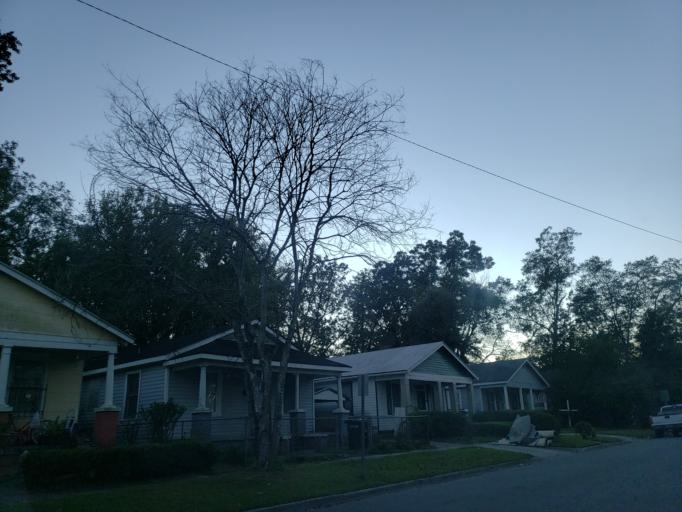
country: US
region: Georgia
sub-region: Chatham County
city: Savannah
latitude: 32.0583
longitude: -81.0885
